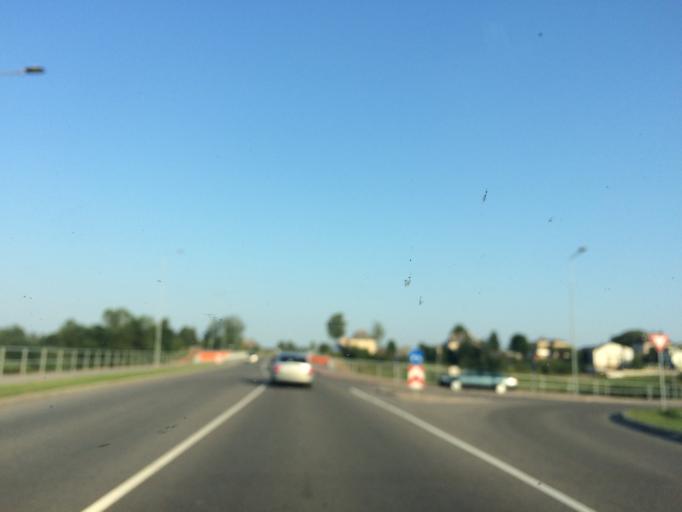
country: LV
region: Rezekne
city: Rezekne
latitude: 56.5143
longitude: 27.3538
